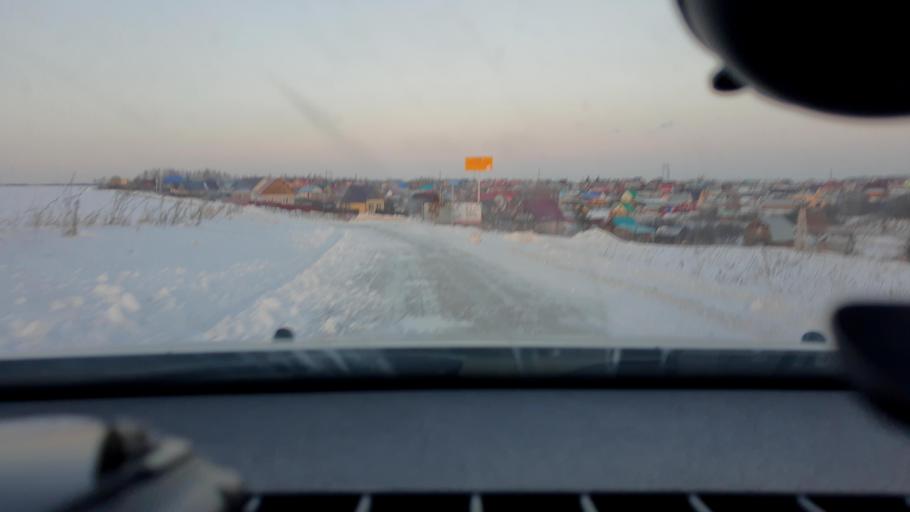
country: RU
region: Bashkortostan
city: Iglino
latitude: 54.8587
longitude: 56.4698
